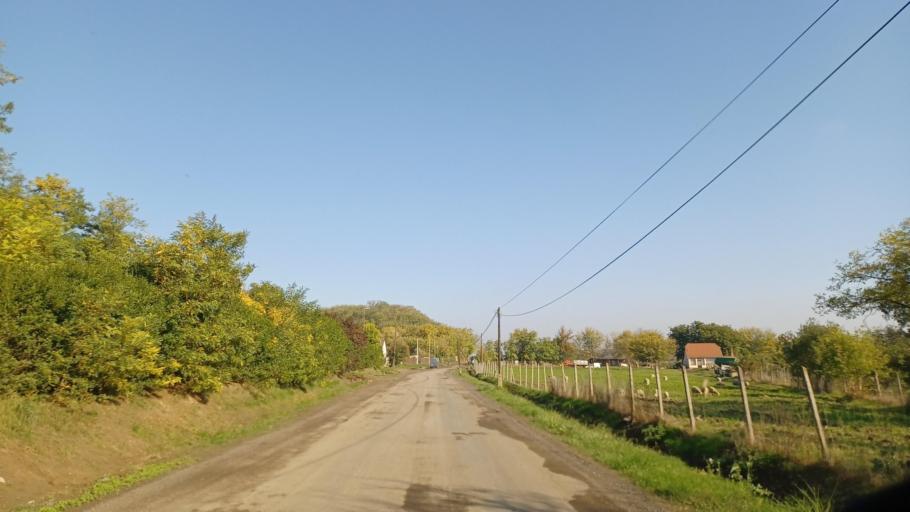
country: HU
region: Tolna
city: Szedres
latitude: 46.5168
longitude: 18.5910
